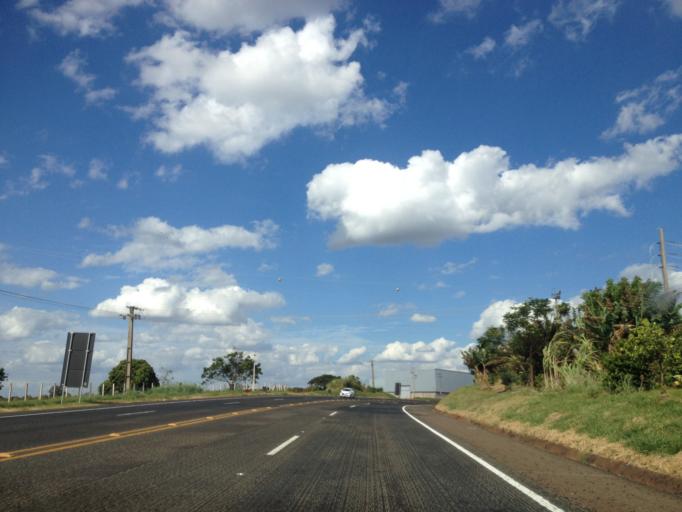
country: BR
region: Parana
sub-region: Mandaguari
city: Mandaguari
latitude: -23.5072
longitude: -51.6803
